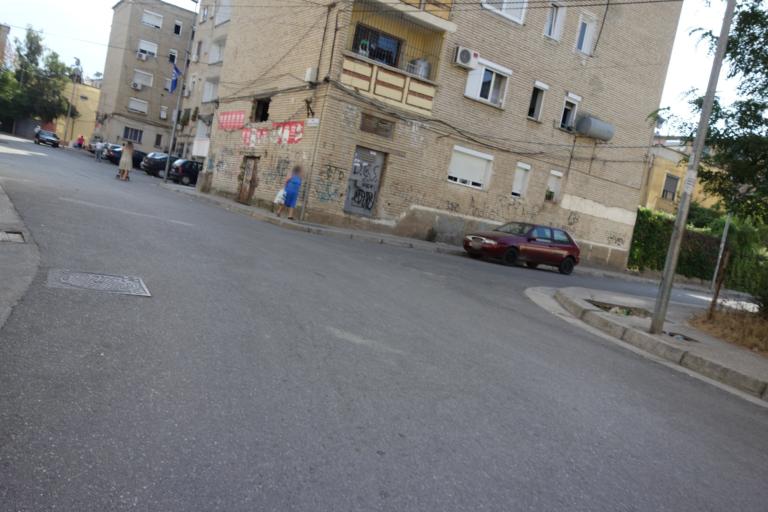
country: AL
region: Tirane
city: Tirana
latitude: 41.3388
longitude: 19.8413
